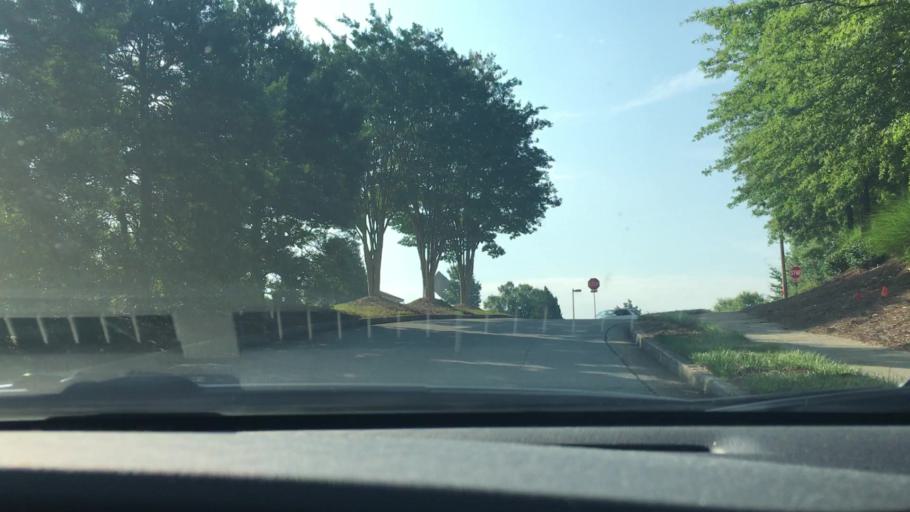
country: US
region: Georgia
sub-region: Cobb County
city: Kennesaw
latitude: 34.0033
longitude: -84.5672
